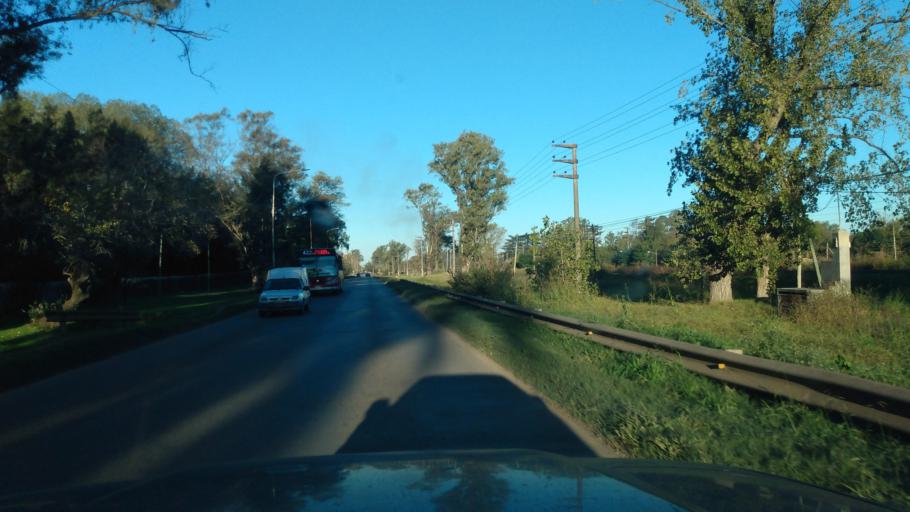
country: AR
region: Buenos Aires
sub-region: Partido de General Rodriguez
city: General Rodriguez
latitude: -34.6345
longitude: -58.8459
